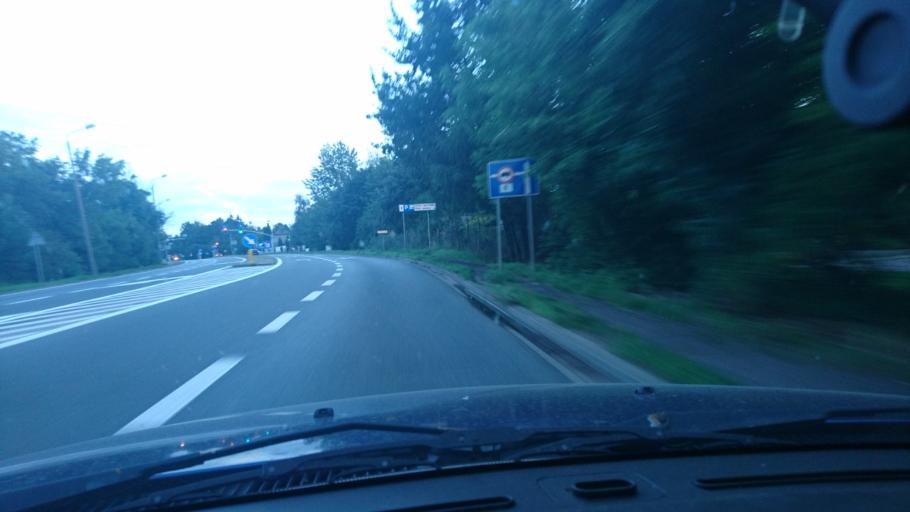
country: PL
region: Silesian Voivodeship
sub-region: Powiat tarnogorski
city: Tarnowskie Gory
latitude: 50.4438
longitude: 18.8356
